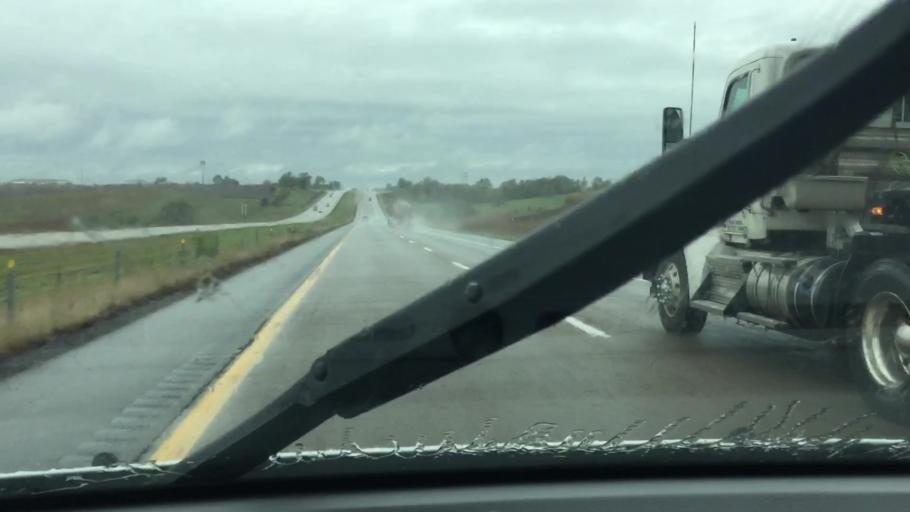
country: US
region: Iowa
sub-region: Poweshiek County
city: Brooklyn
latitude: 41.6956
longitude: -92.3413
